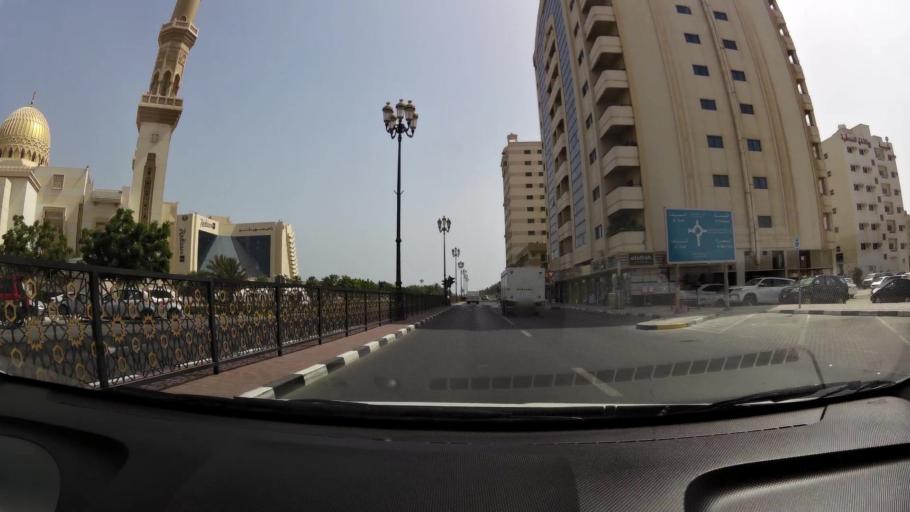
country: AE
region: Ash Shariqah
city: Sharjah
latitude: 25.3685
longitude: 55.3913
